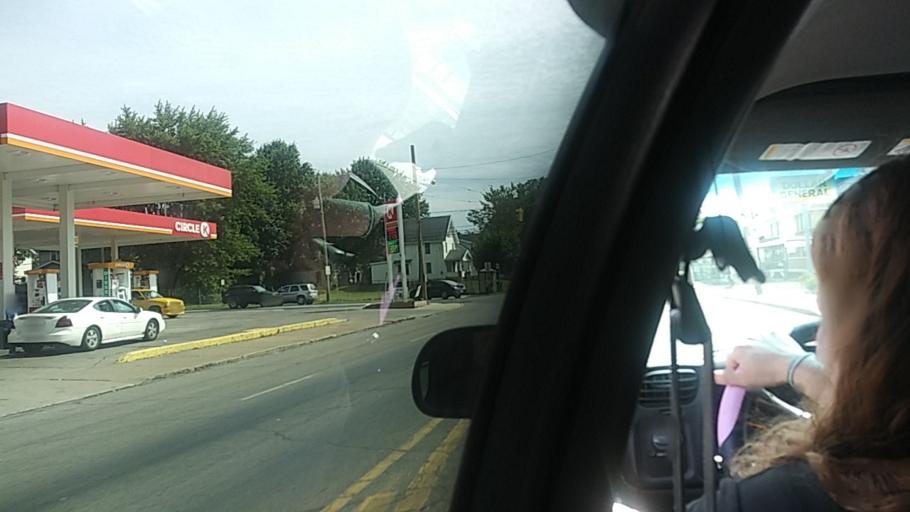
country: US
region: Ohio
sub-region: Summit County
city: Akron
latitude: 41.0549
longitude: -81.5100
